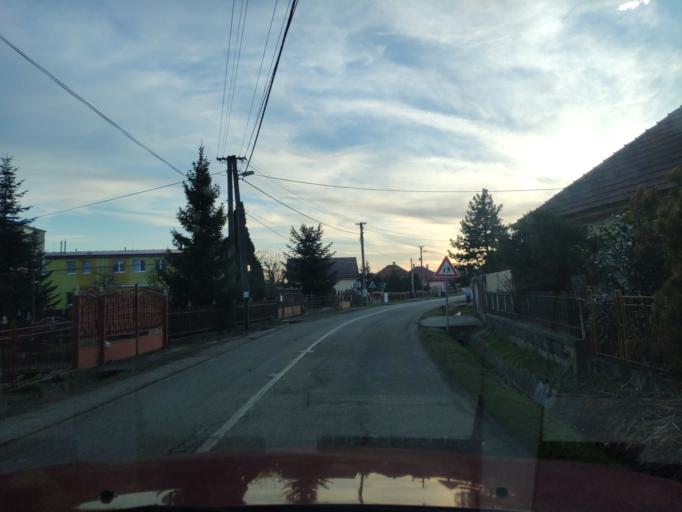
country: SK
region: Kosicky
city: Kosice
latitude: 48.7032
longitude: 21.4124
